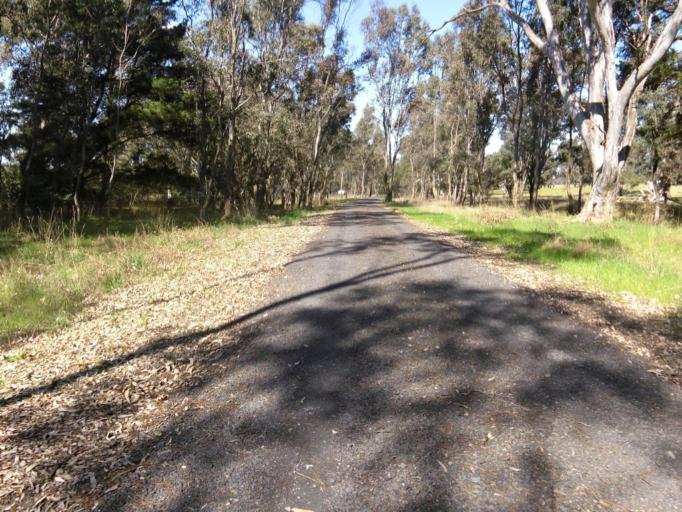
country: AU
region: Victoria
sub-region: Murrindindi
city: Alexandra
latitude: -36.9879
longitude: 145.7341
